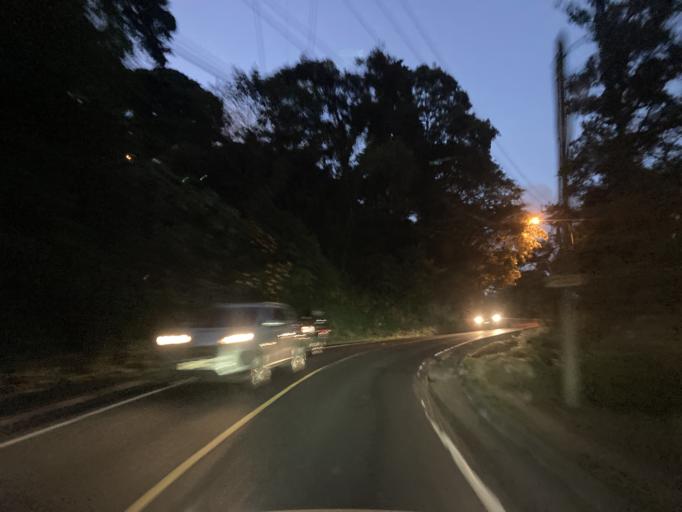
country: GT
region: Guatemala
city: Santa Catarina Pinula
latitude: 14.5956
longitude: -90.4649
